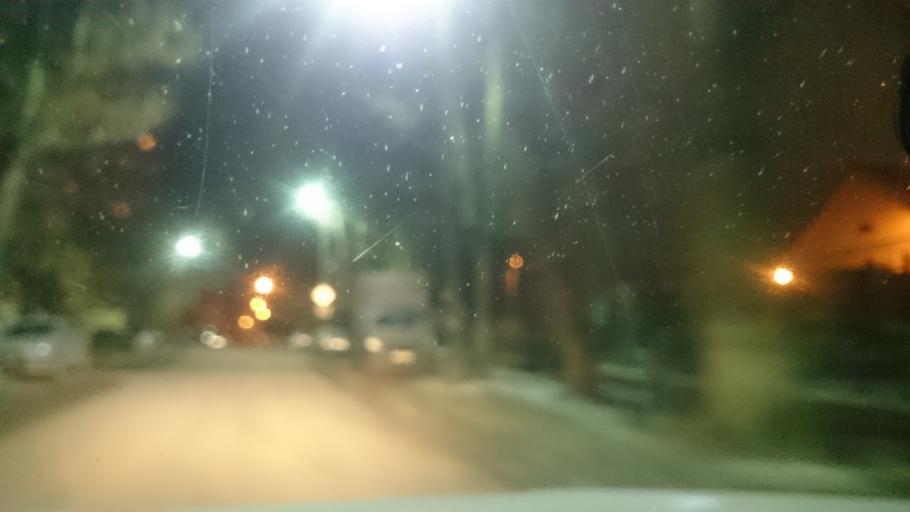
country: RU
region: Tula
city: Tula
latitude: 54.1830
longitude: 37.6322
